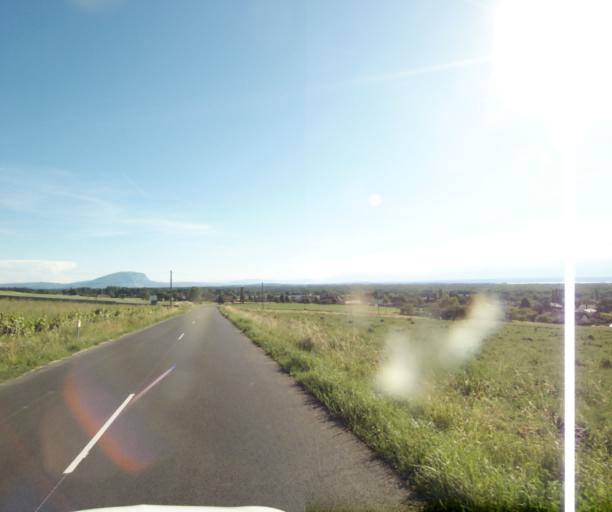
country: FR
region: Rhone-Alpes
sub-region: Departement de la Haute-Savoie
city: Loisin
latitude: 46.2909
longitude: 6.3159
